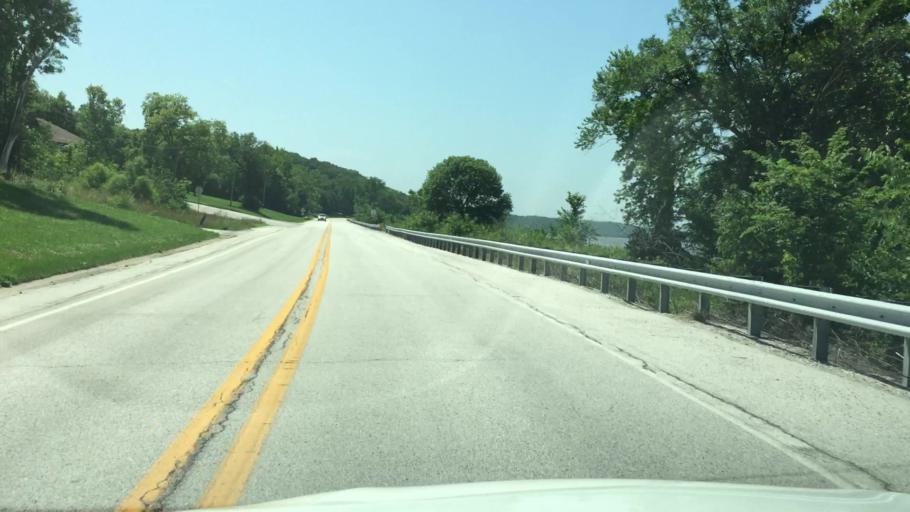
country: US
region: Illinois
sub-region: Hancock County
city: Nauvoo
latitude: 40.5129
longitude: -91.3594
